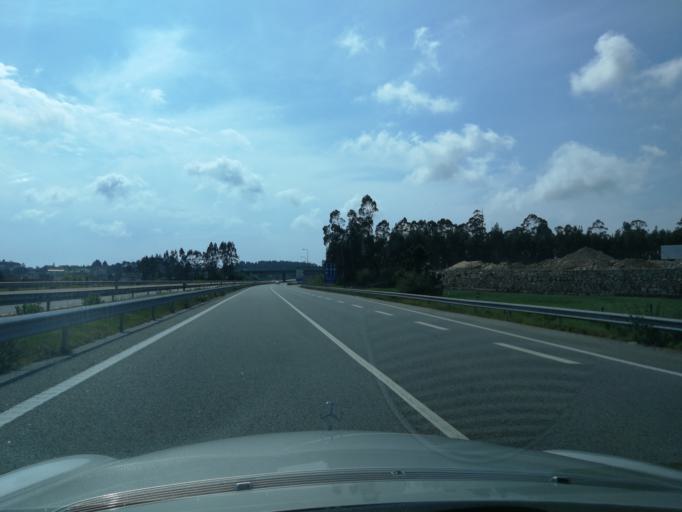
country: PT
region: Porto
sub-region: Vila do Conde
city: Arvore
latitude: 41.3900
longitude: -8.6932
